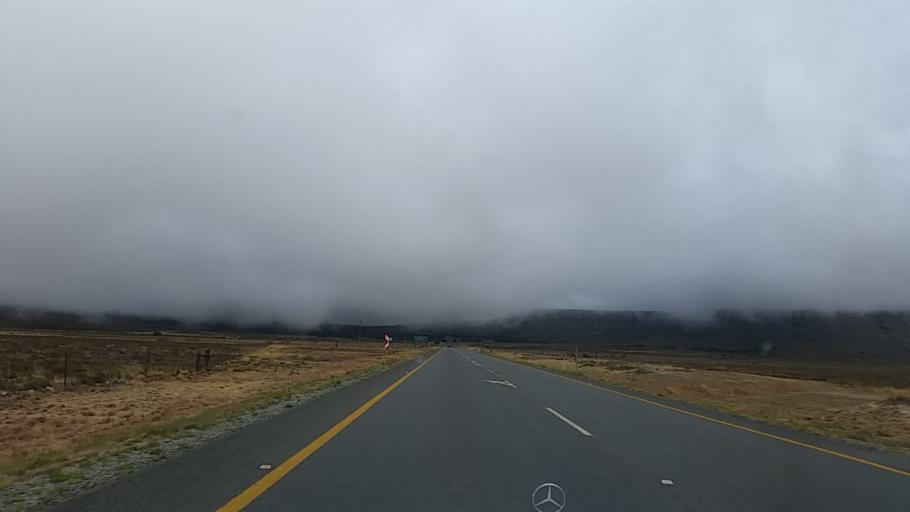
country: ZA
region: Eastern Cape
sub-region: Cacadu District Municipality
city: Graaff-Reinet
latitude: -31.9297
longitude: 24.7450
